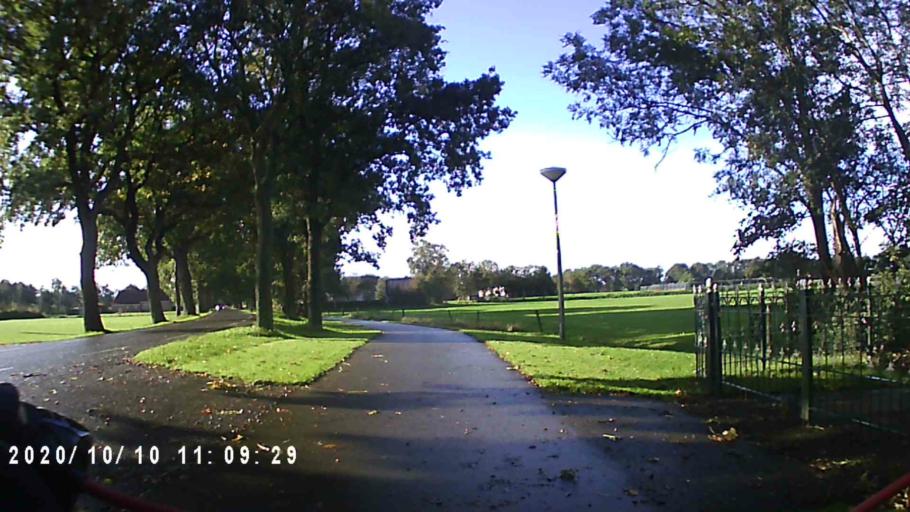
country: NL
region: Friesland
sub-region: Gemeente Smallingerland
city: Drachtstercompagnie
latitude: 53.1184
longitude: 6.2077
